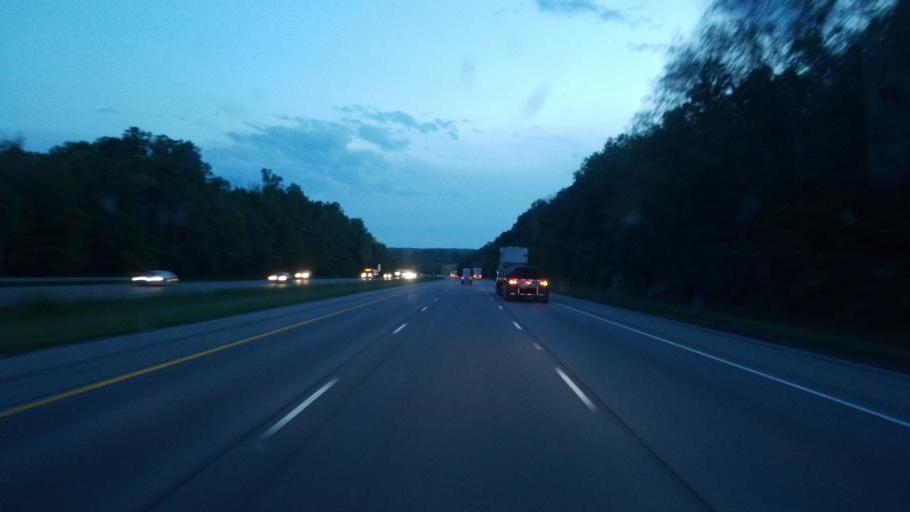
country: US
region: Ohio
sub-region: Knox County
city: Fredericktown
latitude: 40.5633
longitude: -82.6346
